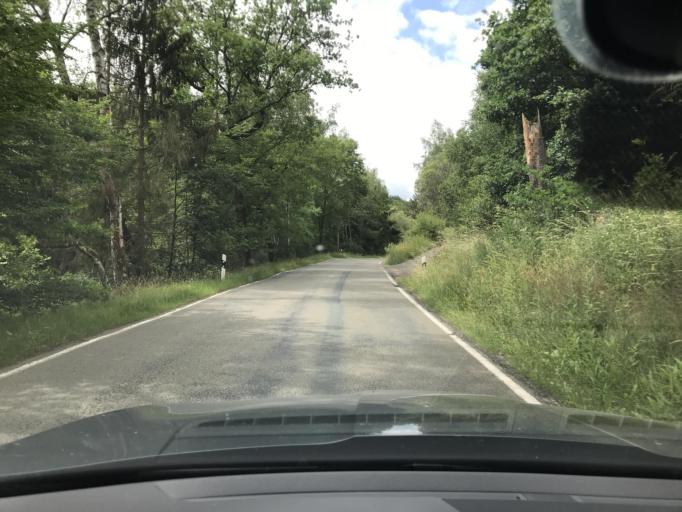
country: DE
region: Saxony-Anhalt
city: Harzgerode
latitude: 51.6278
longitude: 11.0884
